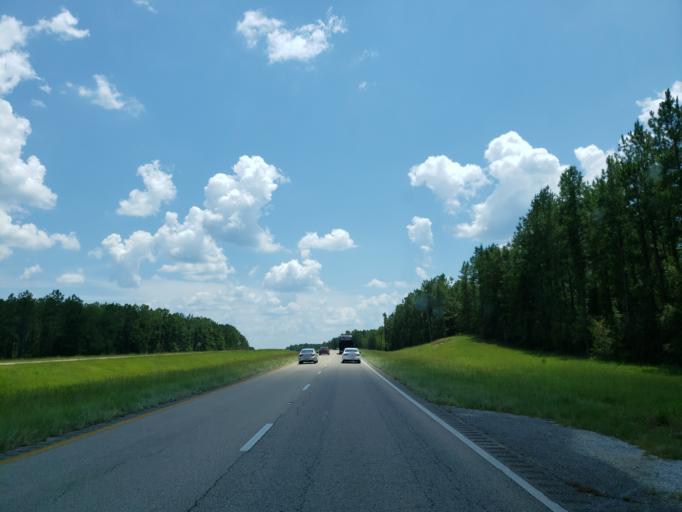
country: US
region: Mississippi
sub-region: Wayne County
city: Belmont
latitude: 31.4927
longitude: -88.4922
